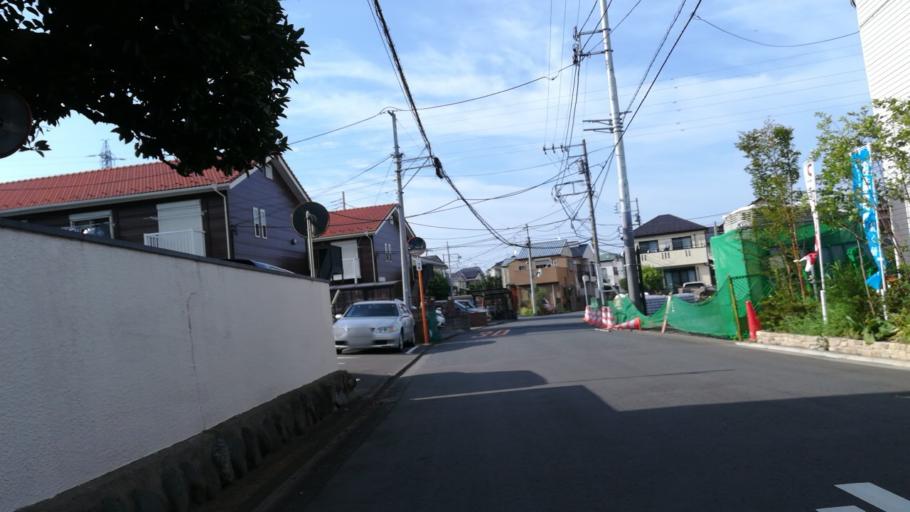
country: JP
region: Tokyo
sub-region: Machida-shi
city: Machida
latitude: 35.5712
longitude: 139.4084
